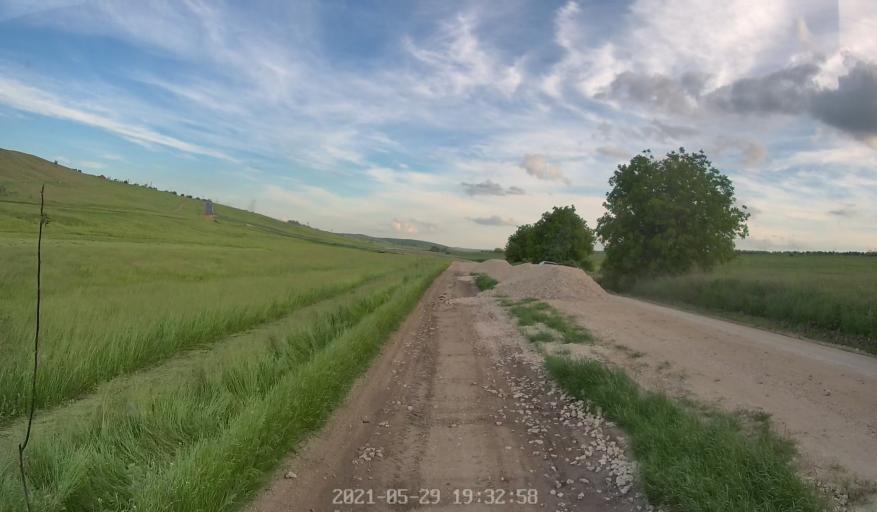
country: MD
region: Chisinau
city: Singera
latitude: 46.8315
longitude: 28.9563
